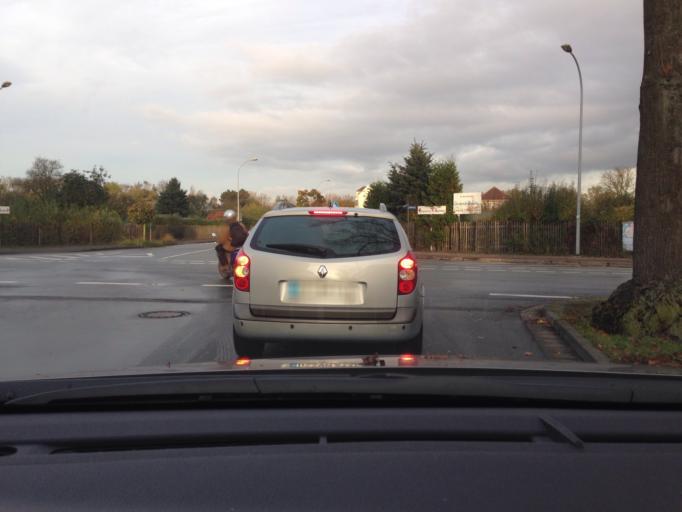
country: DE
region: Saxony
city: Taucha
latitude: 51.3366
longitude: 12.4671
